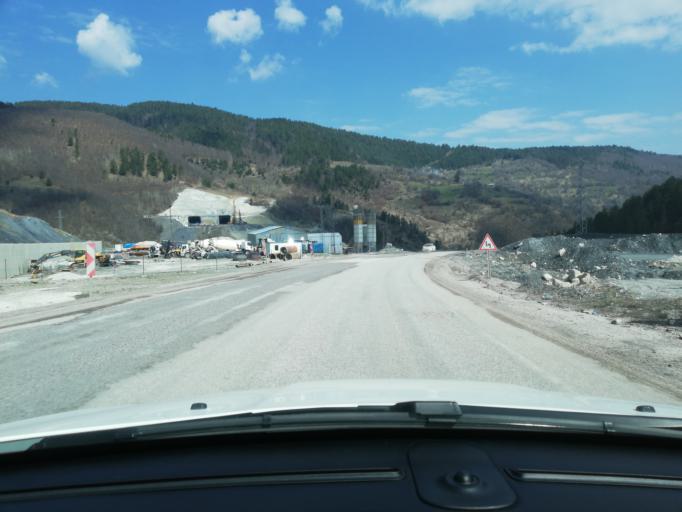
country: TR
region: Kastamonu
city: Kuzyaka
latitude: 41.1100
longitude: 33.7503
